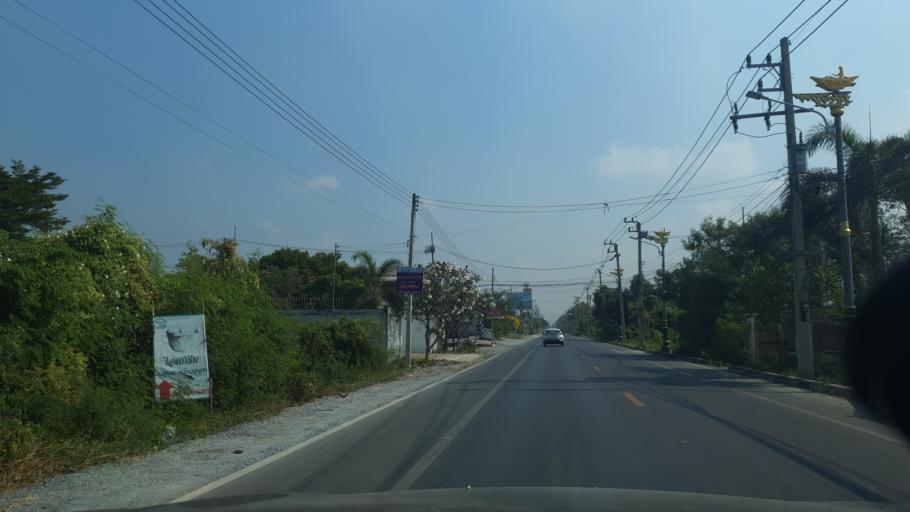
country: TH
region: Nakhon Pathom
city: Salaya
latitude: 13.7728
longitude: 100.2915
